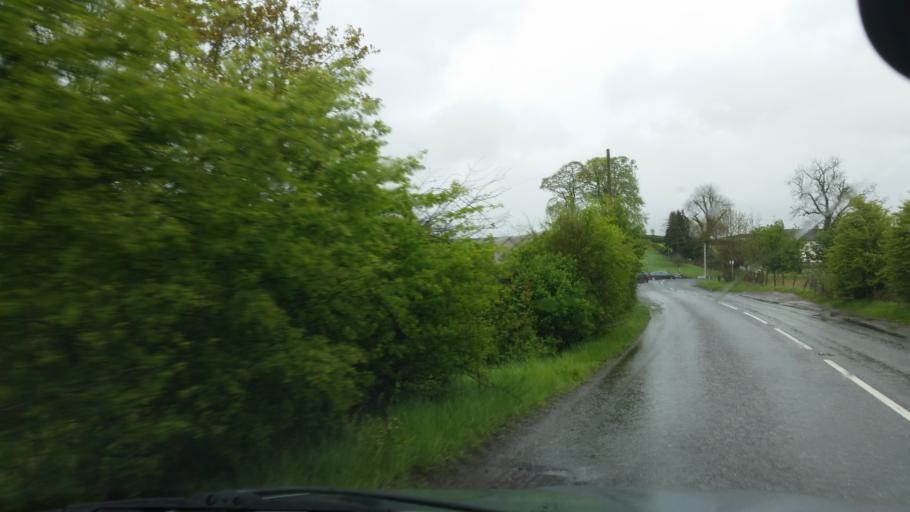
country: GB
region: Northern Ireland
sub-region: Omagh District
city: Omagh
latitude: 54.5730
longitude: -7.2775
